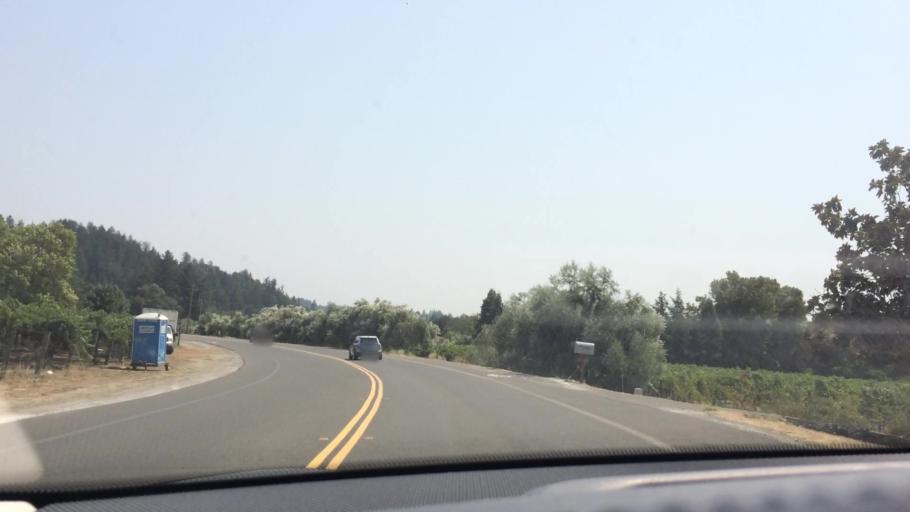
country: US
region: California
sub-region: Napa County
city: Deer Park
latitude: 38.5637
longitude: -122.5132
